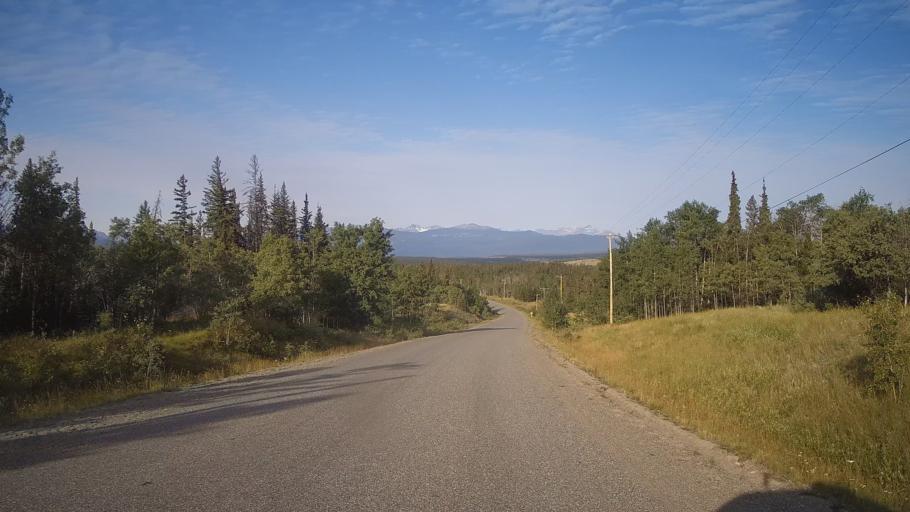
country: CA
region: British Columbia
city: Hanceville
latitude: 51.9499
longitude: -124.4495
